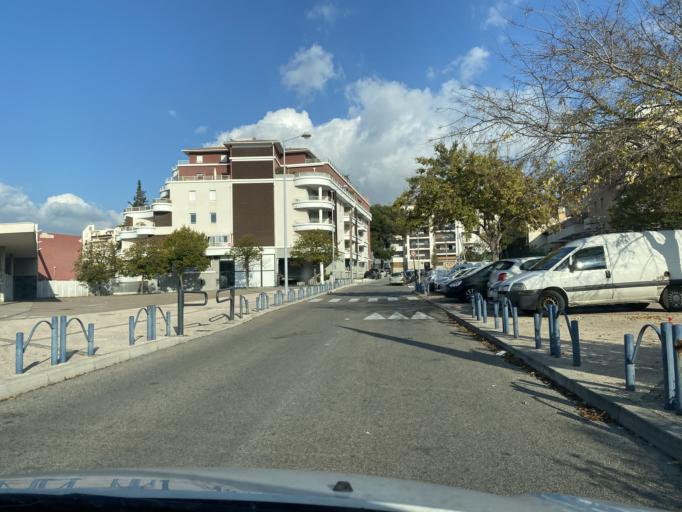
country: FR
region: Provence-Alpes-Cote d'Azur
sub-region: Departement du Var
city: La Seyne-sur-Mer
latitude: 43.1125
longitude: 5.8701
